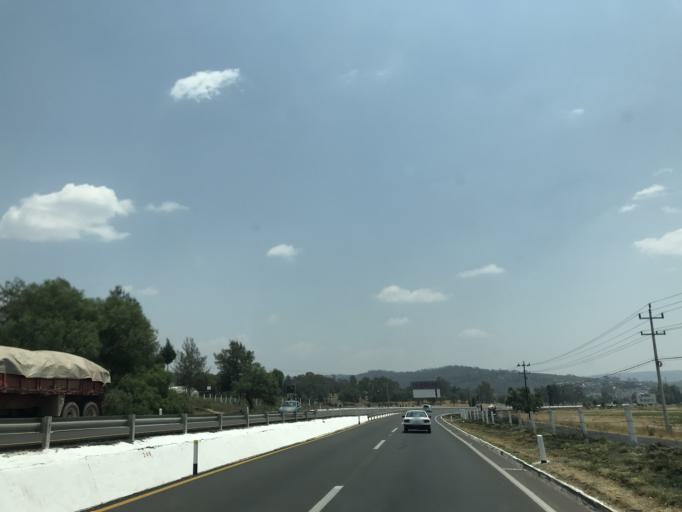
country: MX
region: Tlaxcala
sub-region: Ixtacuixtla de Mariano Matamoros
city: Villa Mariano Matamoros
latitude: 19.3261
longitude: -98.3663
